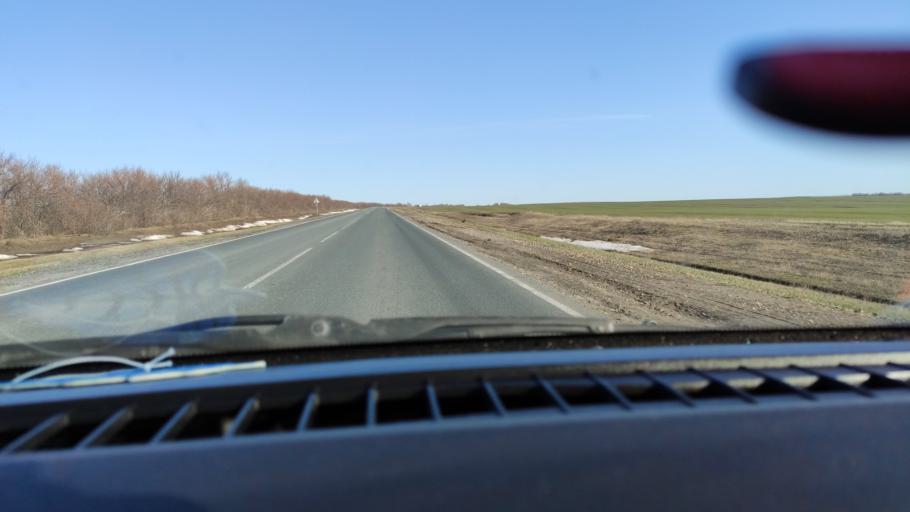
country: RU
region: Saratov
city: Dukhovnitskoye
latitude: 52.7601
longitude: 48.2418
